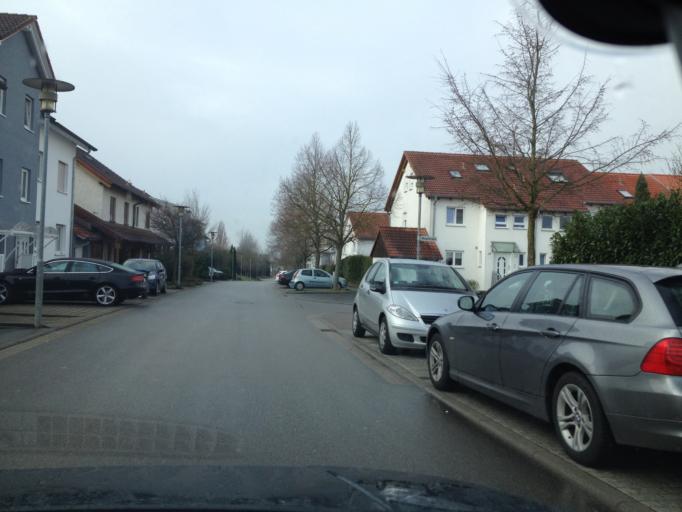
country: DE
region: Baden-Wuerttemberg
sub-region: Regierungsbezirk Stuttgart
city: Oedheim
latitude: 49.2098
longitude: 9.2585
